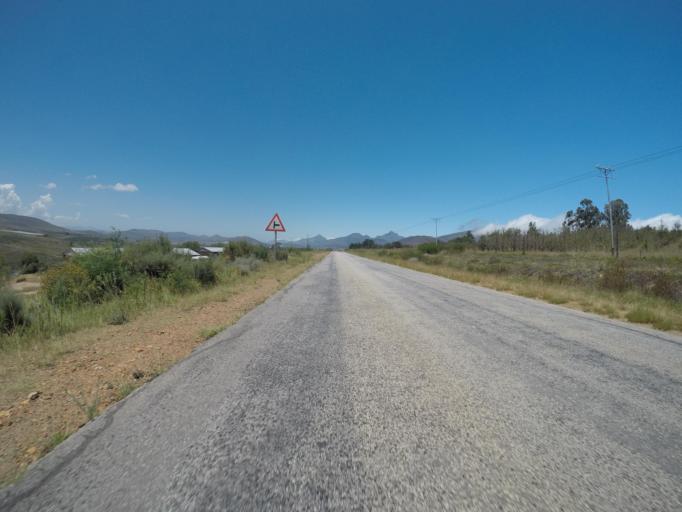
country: ZA
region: Western Cape
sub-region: Eden District Municipality
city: Plettenberg Bay
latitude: -33.7741
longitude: 23.5844
